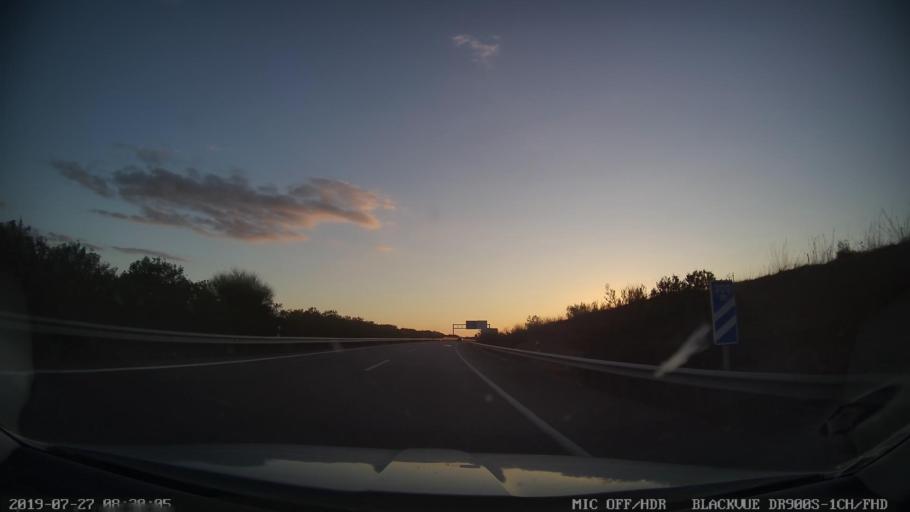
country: ES
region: Extremadura
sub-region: Provincia de Badajoz
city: Valdelacalzada
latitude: 38.8480
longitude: -6.7073
